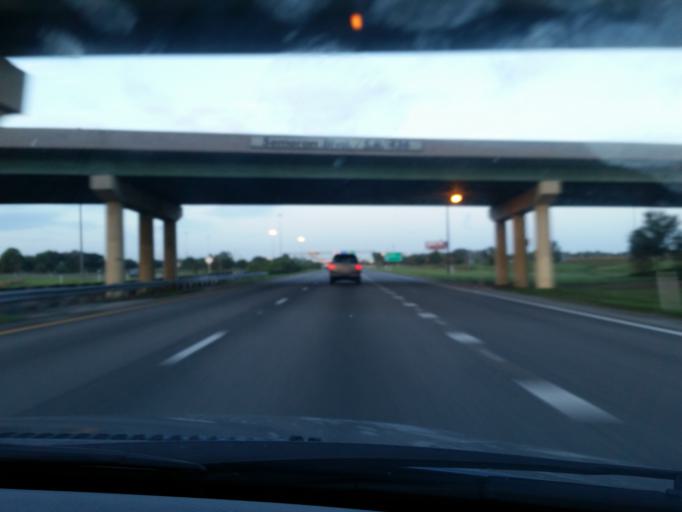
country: US
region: Florida
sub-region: Orange County
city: Belle Isle
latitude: 28.4516
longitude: -81.3087
